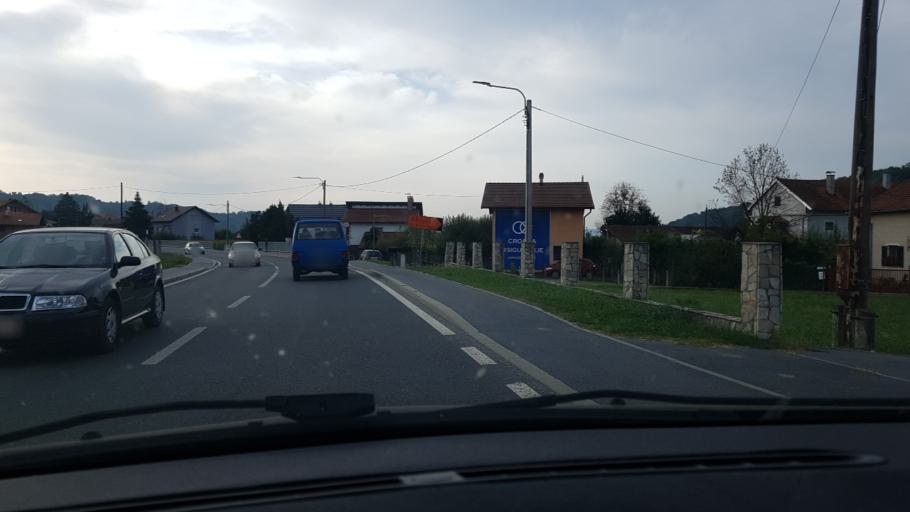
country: HR
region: Krapinsko-Zagorska
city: Zlatar
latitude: 46.0984
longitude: 16.0684
